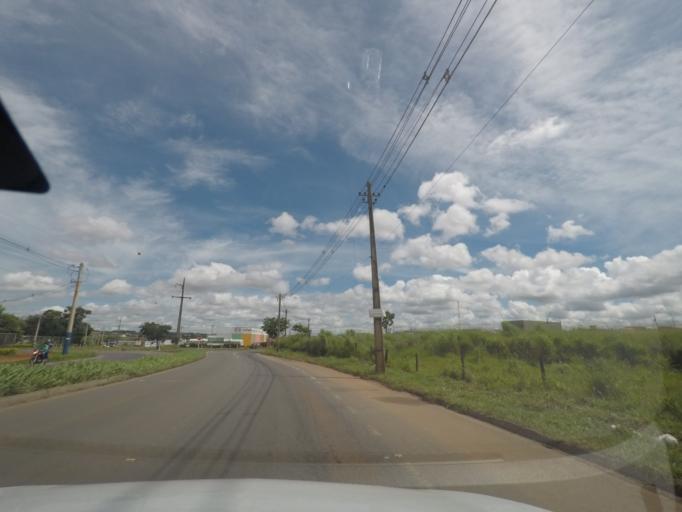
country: BR
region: Goias
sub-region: Goiania
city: Goiania
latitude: -16.7156
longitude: -49.3572
